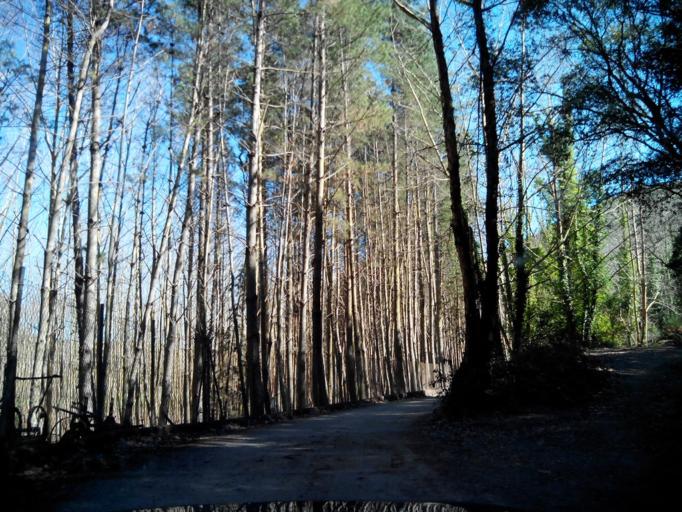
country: ES
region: Catalonia
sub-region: Provincia de Barcelona
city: Dosrius
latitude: 41.6050
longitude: 2.4564
